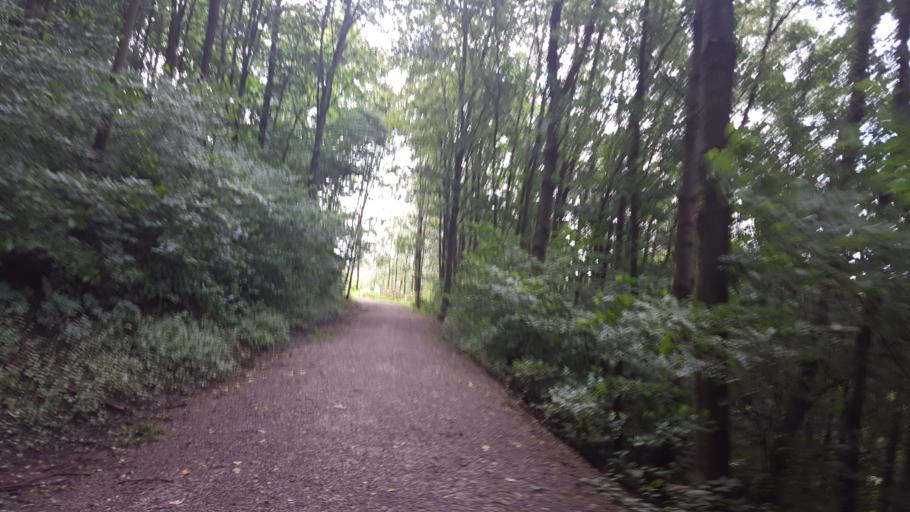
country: DE
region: North Rhine-Westphalia
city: Oer-Erkenschwick
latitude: 51.6476
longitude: 7.2631
